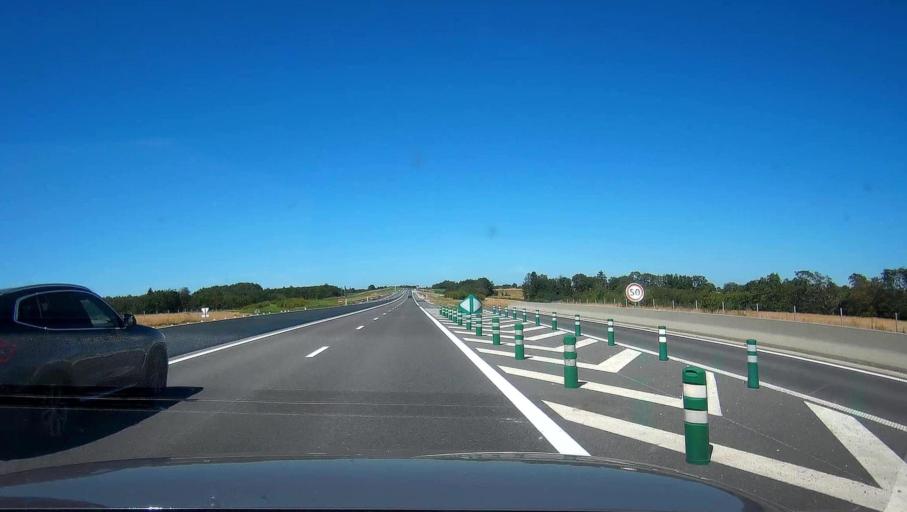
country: FR
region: Champagne-Ardenne
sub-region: Departement des Ardennes
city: Rocroi
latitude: 49.9005
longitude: 4.5218
